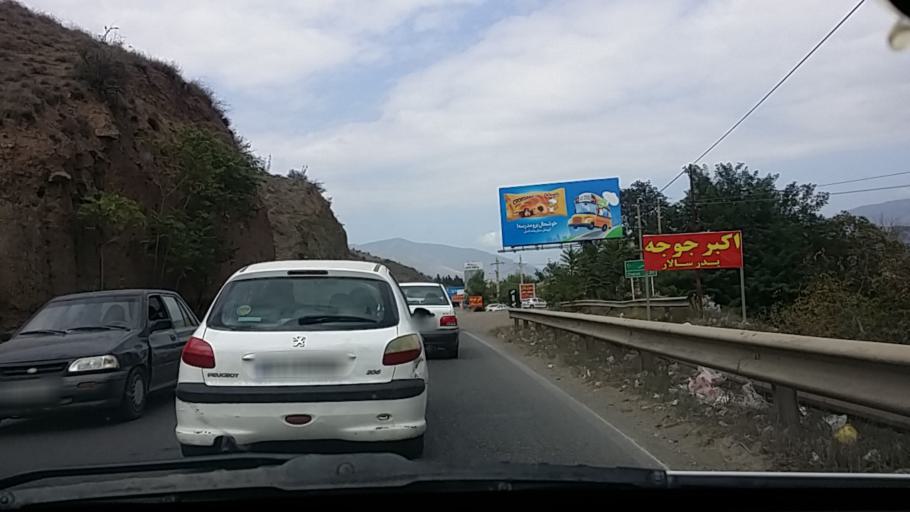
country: IR
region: Mazandaran
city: Chalus
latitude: 36.4329
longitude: 51.2880
